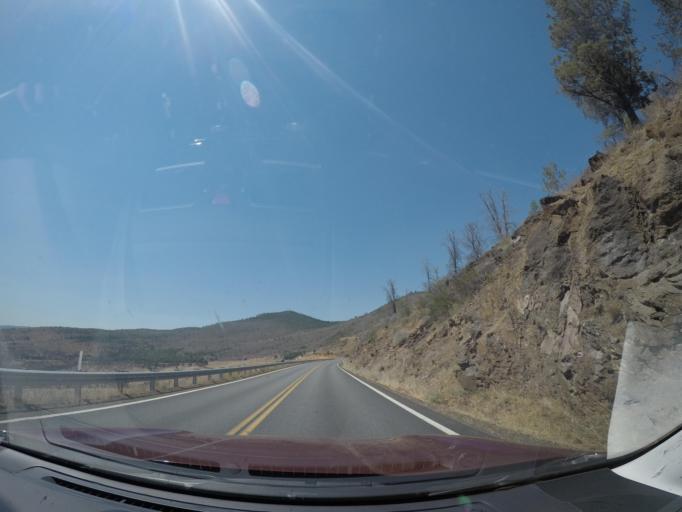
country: US
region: California
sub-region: Shasta County
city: Burney
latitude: 40.9958
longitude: -121.4953
